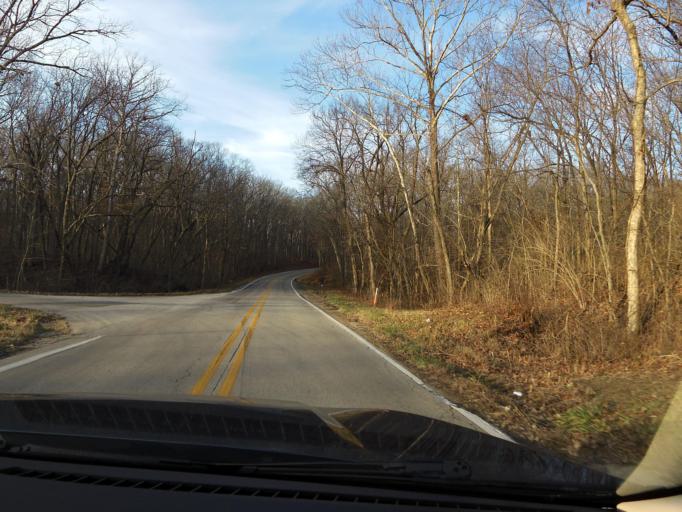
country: US
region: Illinois
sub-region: Fayette County
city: Vandalia
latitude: 38.9221
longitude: -89.2304
